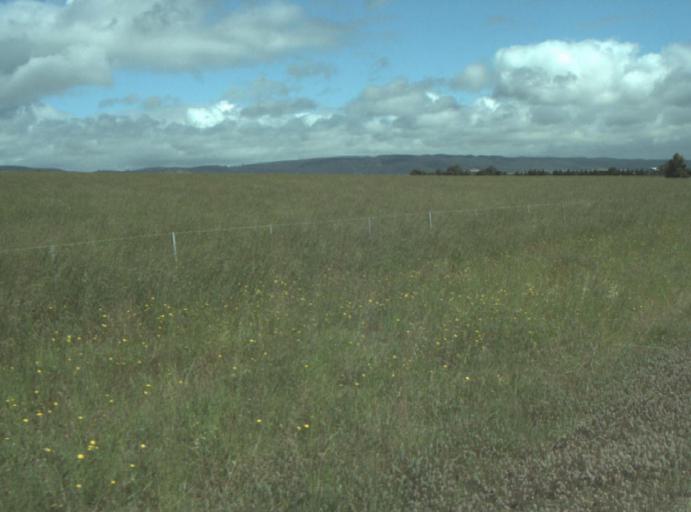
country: AU
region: Victoria
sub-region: Greater Geelong
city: Lara
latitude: -37.8679
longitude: 144.3238
